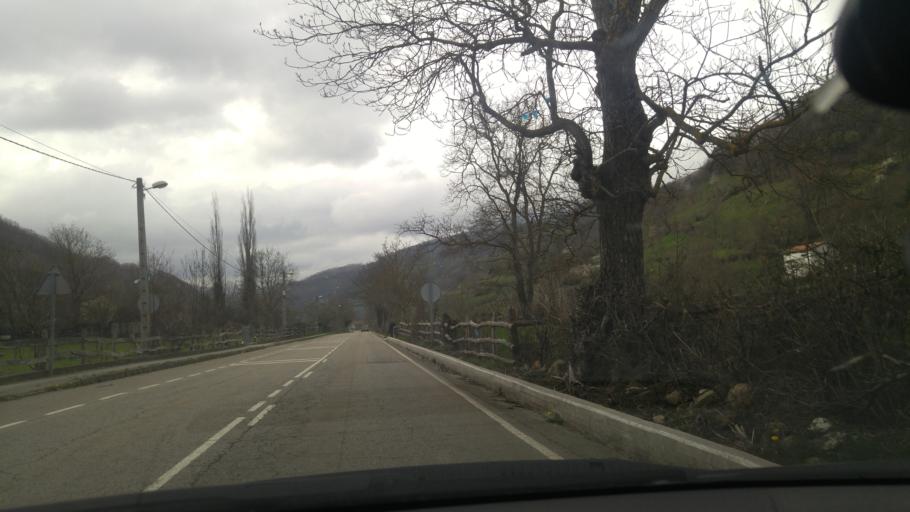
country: ES
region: Asturias
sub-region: Province of Asturias
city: Rio Aller
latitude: 43.1086
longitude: -5.5223
